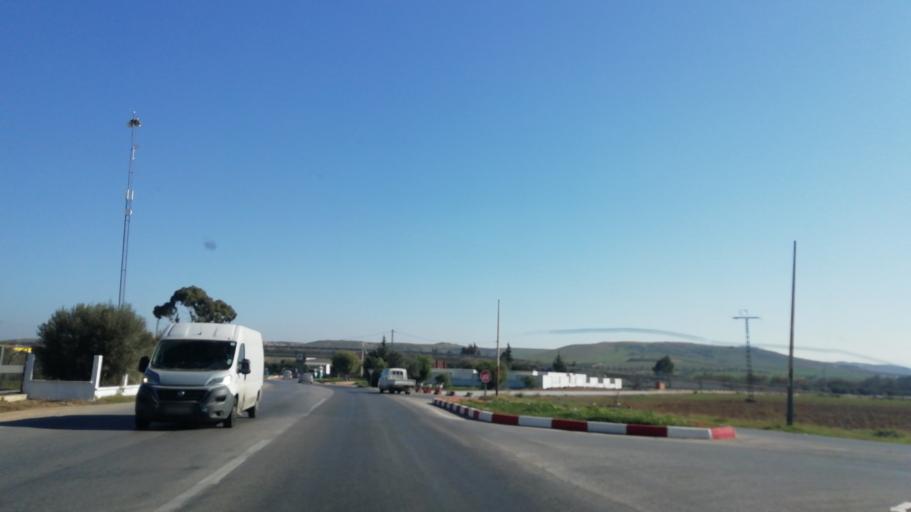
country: DZ
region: Tlemcen
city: Remchi
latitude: 35.0472
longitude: -1.5058
